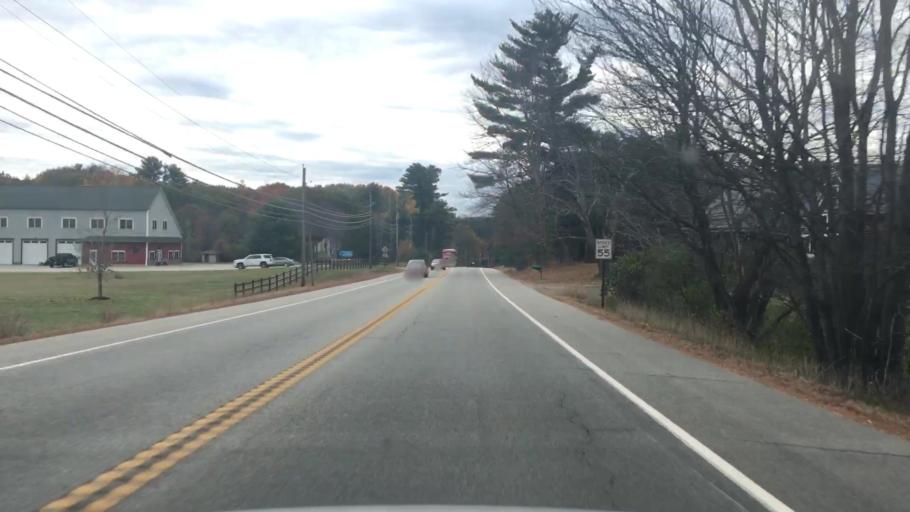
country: US
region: Maine
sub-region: York County
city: Alfred
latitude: 43.4760
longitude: -70.6939
